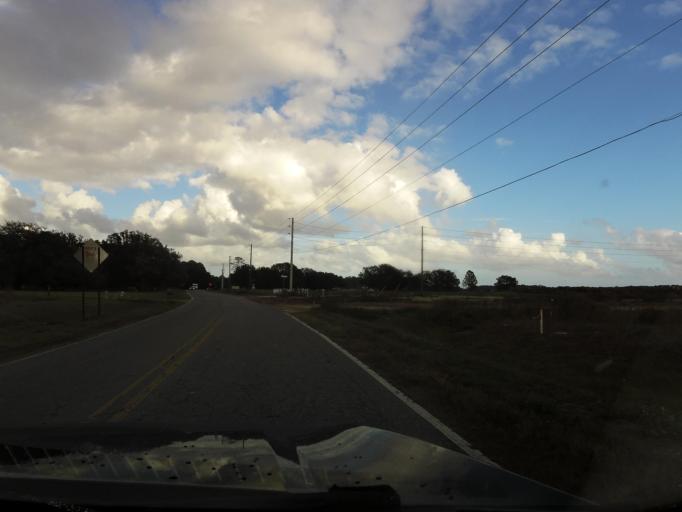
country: US
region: Florida
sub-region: Clay County
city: Asbury Lake
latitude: 30.0465
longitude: -81.7759
